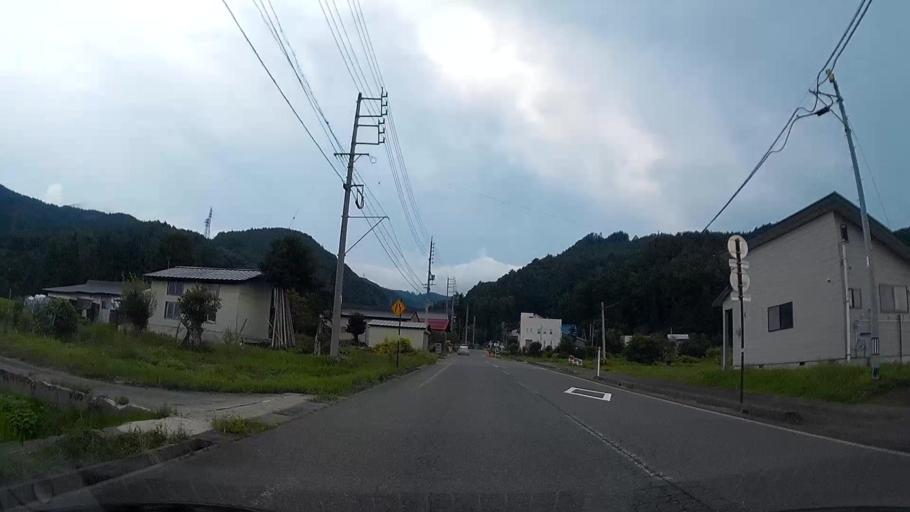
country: JP
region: Nagano
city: Iiyama
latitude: 36.8286
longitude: 138.4186
